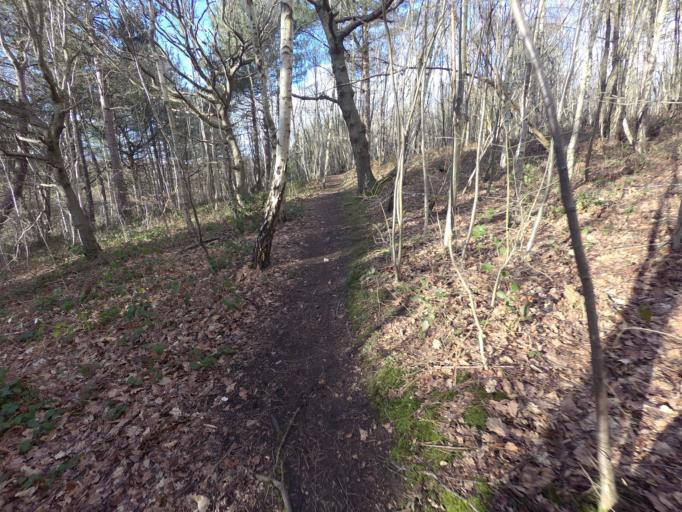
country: GB
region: England
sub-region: Greater London
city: Bexley
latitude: 51.4237
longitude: 0.1599
